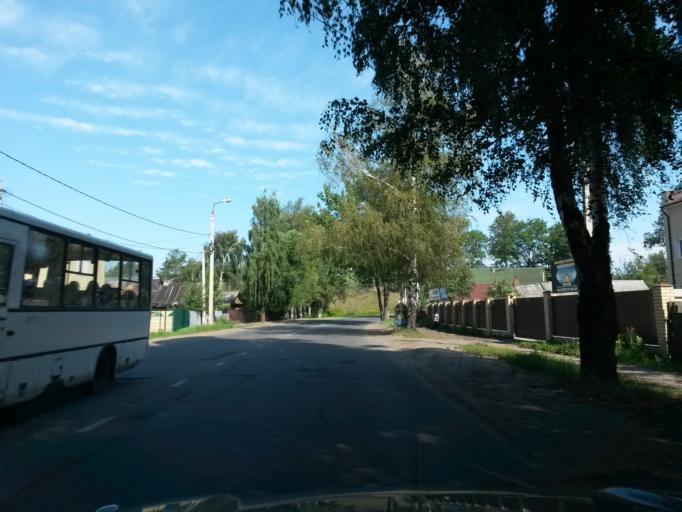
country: RU
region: Jaroslavl
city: Yaroslavl
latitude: 57.6501
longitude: 39.9068
